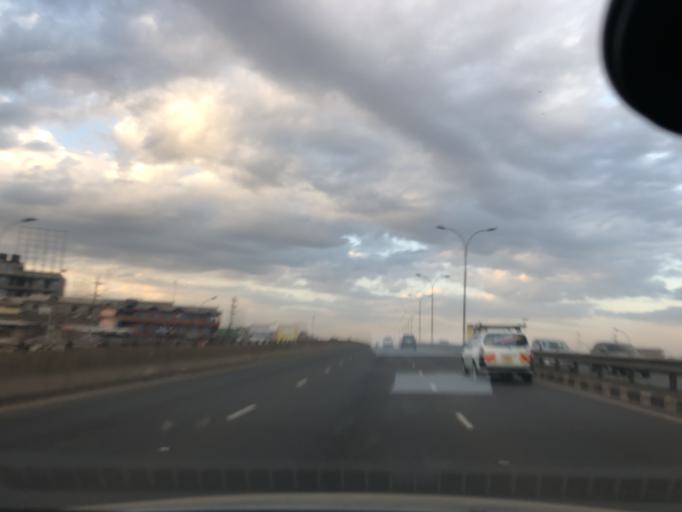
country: KE
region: Kiambu
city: Kiambu
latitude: -1.2055
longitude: 36.9153
